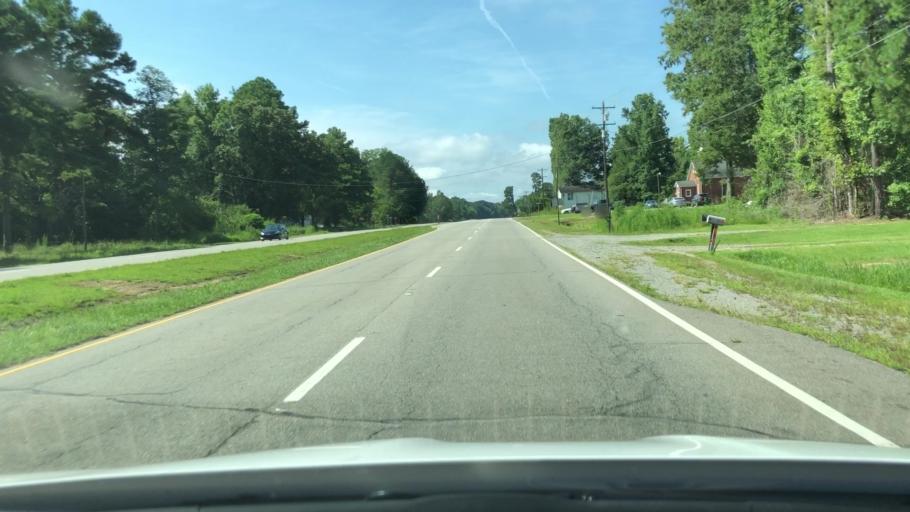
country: US
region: North Carolina
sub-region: Bertie County
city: Windsor
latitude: 35.9532
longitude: -76.9554
